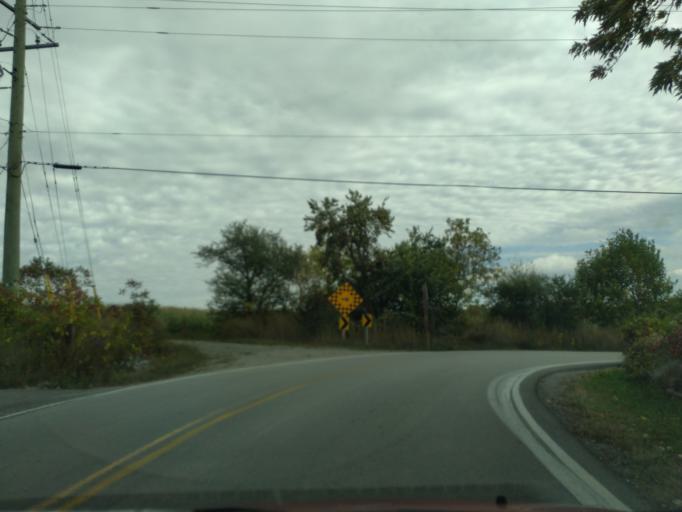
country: CA
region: Ontario
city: Keswick
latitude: 44.2755
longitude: -79.3506
